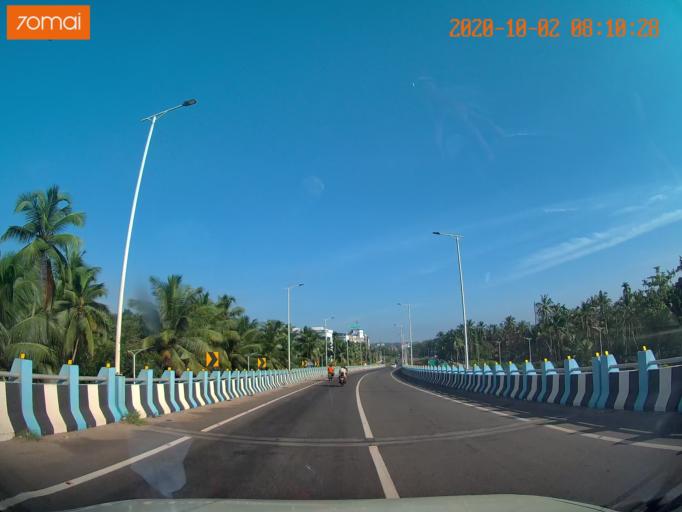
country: IN
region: Kerala
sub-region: Kozhikode
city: Kozhikode
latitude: 11.2662
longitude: 75.8107
